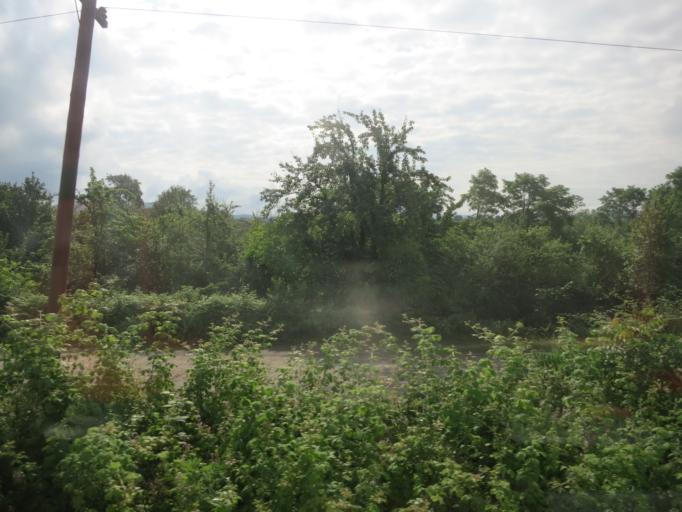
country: GE
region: Guria
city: Urek'i
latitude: 42.0370
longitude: 41.8127
